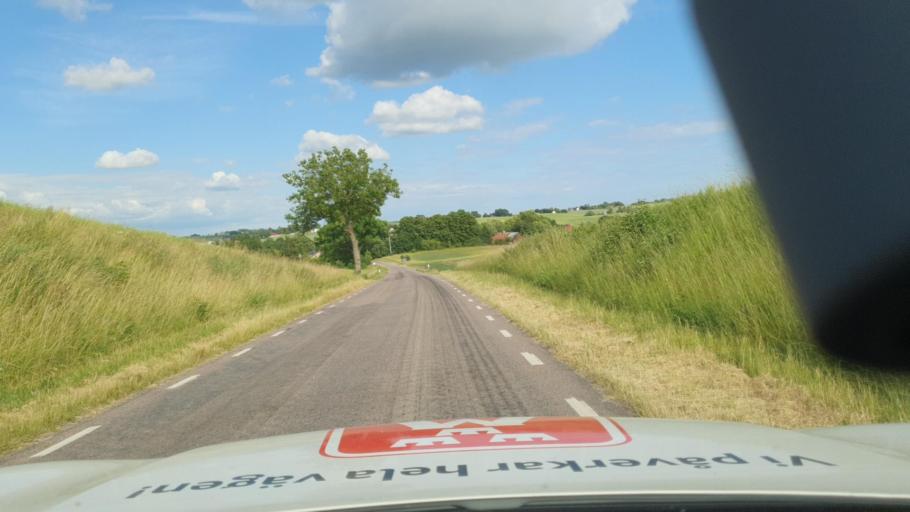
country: SE
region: Skane
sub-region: Skurups Kommun
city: Rydsgard
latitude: 55.4502
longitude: 13.5832
